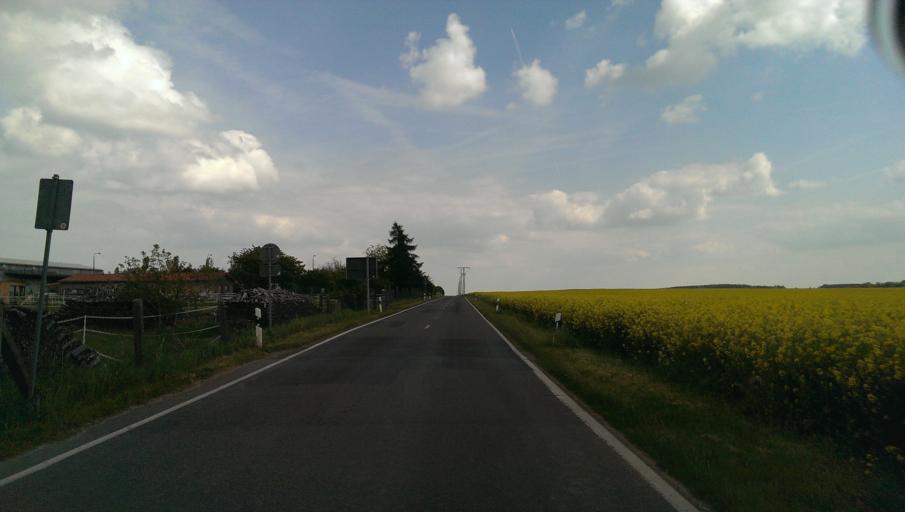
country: DE
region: Brandenburg
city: Belzig
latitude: 52.1010
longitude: 12.5605
